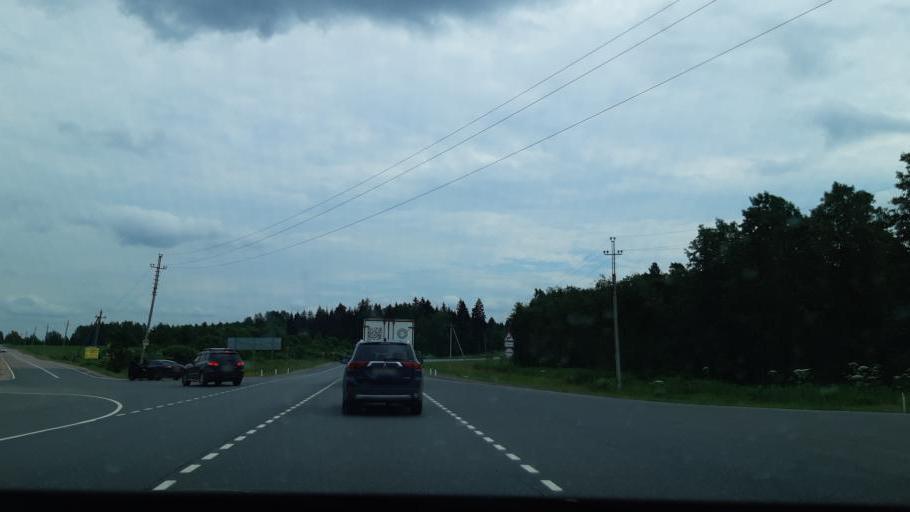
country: RU
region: Moskovskaya
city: Dorokhovo
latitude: 55.4907
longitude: 36.3540
